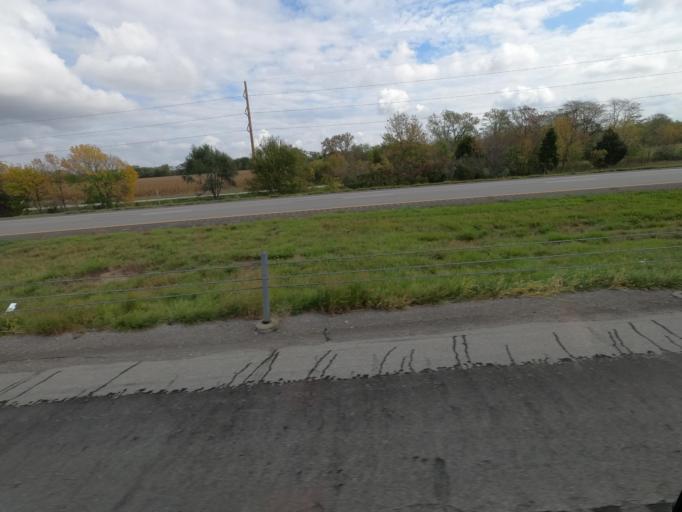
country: US
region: Iowa
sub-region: Story County
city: Huxley
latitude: 41.9436
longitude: -93.5698
